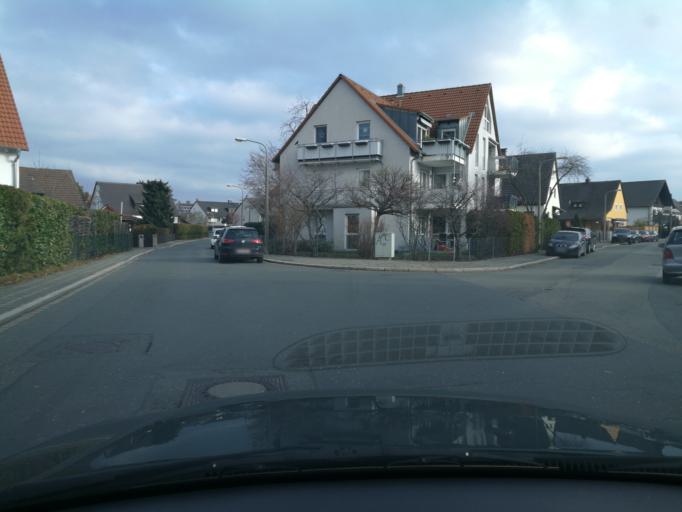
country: DE
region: Bavaria
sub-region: Regierungsbezirk Mittelfranken
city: Grossreuth bei Schweinau
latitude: 49.4544
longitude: 11.0228
